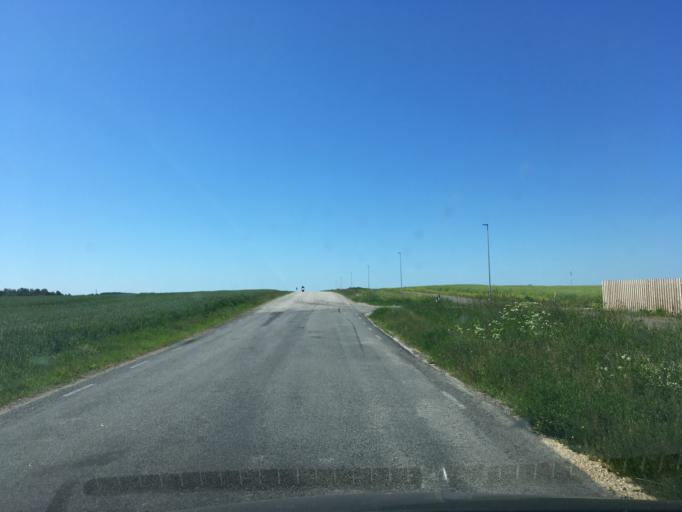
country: EE
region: Harju
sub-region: Raasiku vald
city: Arukula
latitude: 59.4143
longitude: 25.1177
